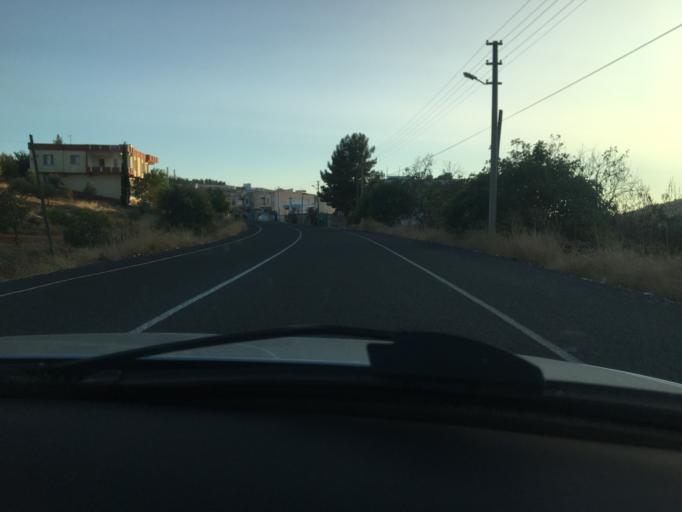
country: TR
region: Sanliurfa
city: Halfeti
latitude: 37.2196
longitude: 37.9543
